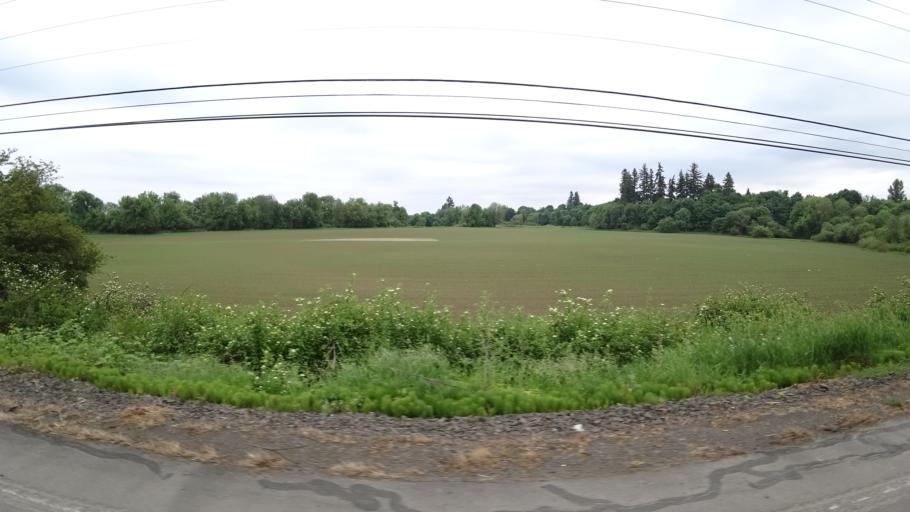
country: US
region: Oregon
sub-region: Washington County
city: Hillsboro
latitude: 45.4978
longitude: -122.9920
